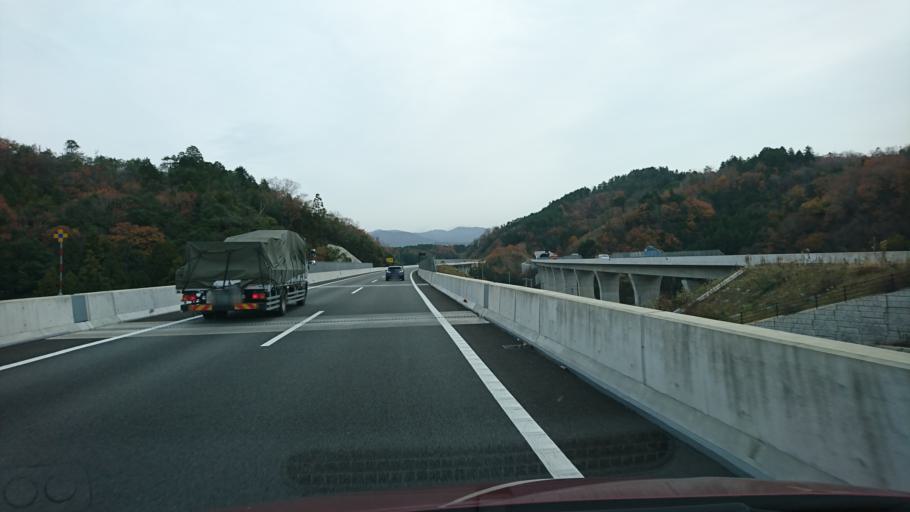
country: JP
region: Hyogo
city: Takarazuka
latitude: 34.8876
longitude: 135.3510
